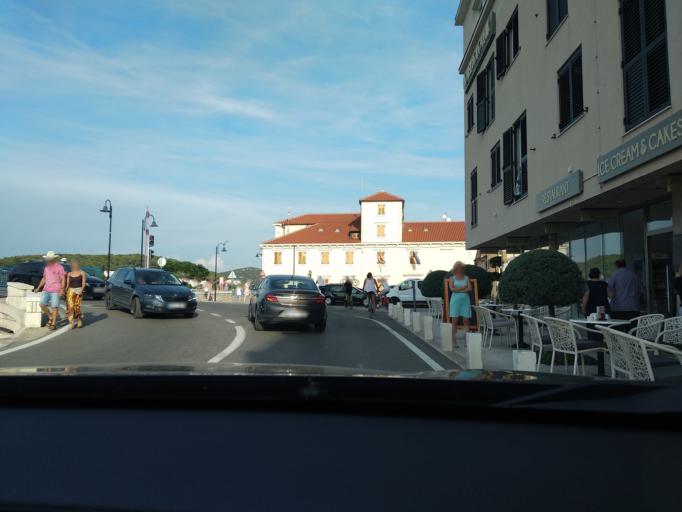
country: HR
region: Sibensko-Kniniska
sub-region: Grad Sibenik
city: Tisno
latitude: 43.8018
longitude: 15.6502
